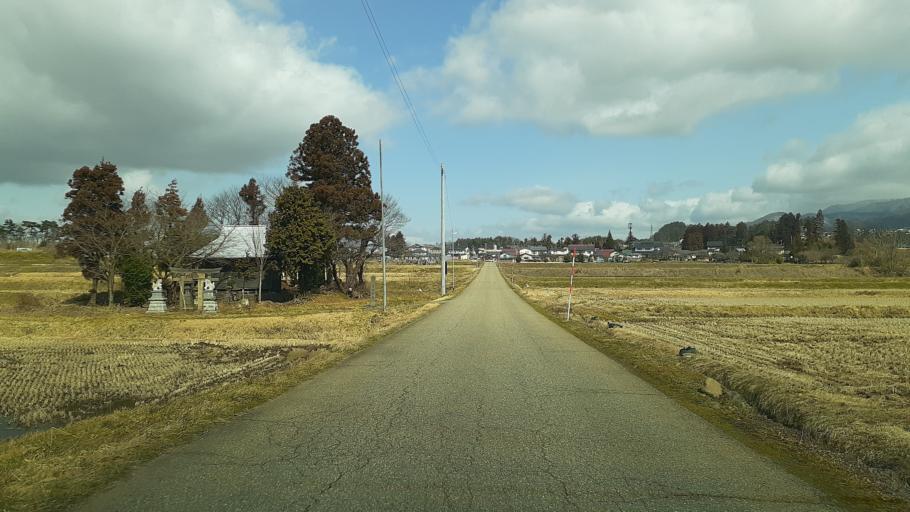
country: JP
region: Fukushima
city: Kitakata
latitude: 37.5477
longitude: 139.9404
